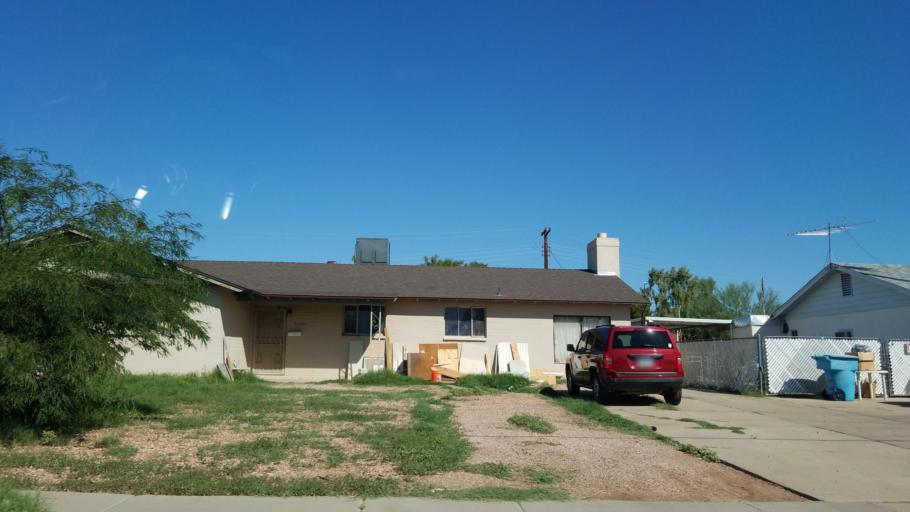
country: US
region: Arizona
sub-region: Maricopa County
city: Glendale
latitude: 33.5023
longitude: -112.1809
